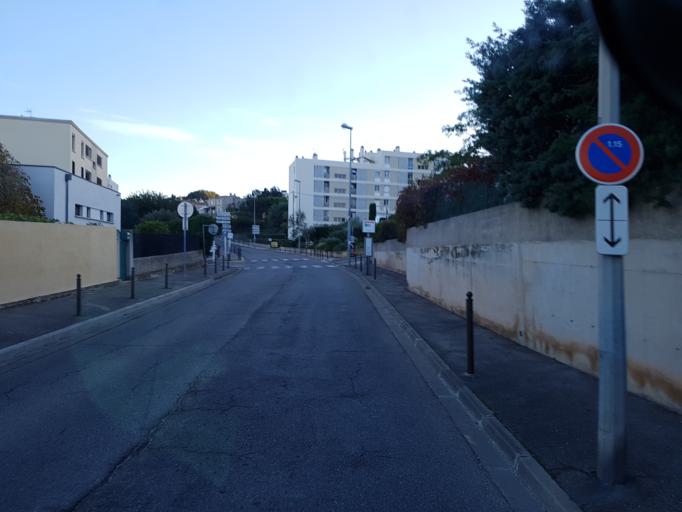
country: FR
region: Provence-Alpes-Cote d'Azur
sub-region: Departement des Bouches-du-Rhone
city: La Ciotat
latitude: 43.1761
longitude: 5.5977
